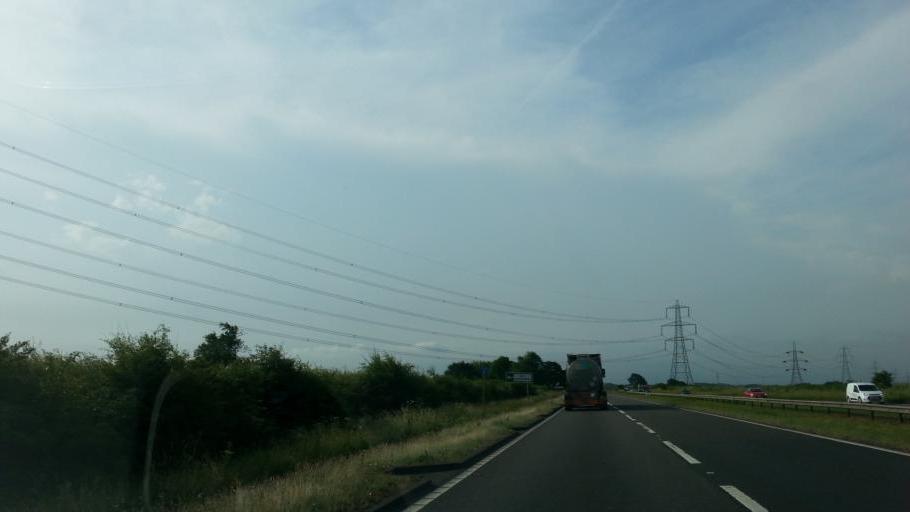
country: GB
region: England
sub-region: Lincolnshire
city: Long Bennington
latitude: 53.0182
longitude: -0.7658
